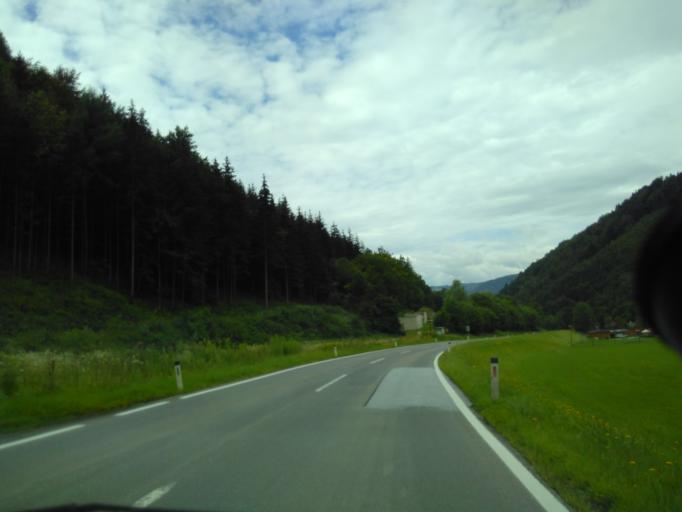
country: AT
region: Styria
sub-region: Politischer Bezirk Graz-Umgebung
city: Schrems bei Frohnleiten
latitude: 47.2748
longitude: 15.3489
